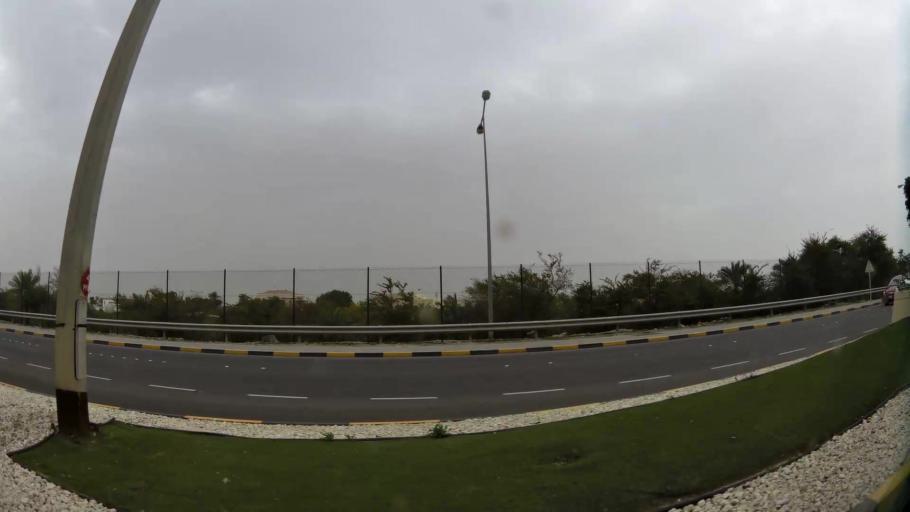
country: BH
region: Northern
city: Ar Rifa'
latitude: 26.1381
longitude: 50.5431
